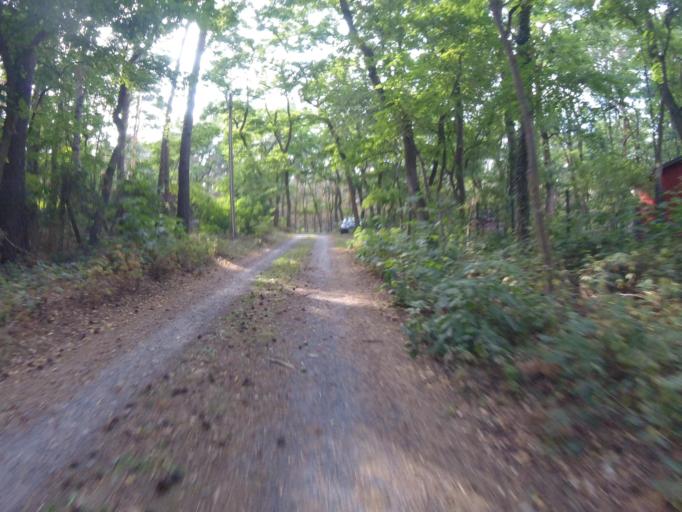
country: DE
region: Brandenburg
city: Munchehofe
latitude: 52.2524
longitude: 13.7838
